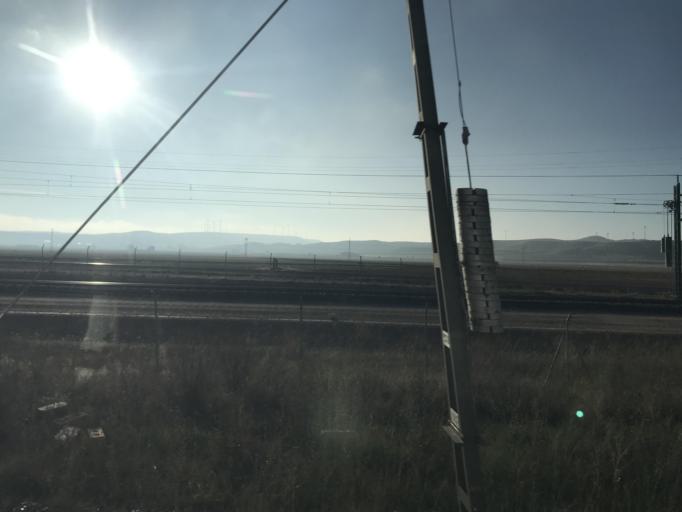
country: ES
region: Castille and Leon
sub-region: Provincia de Palencia
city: Herrera de Valdecanas
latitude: 42.0602
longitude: -4.2294
